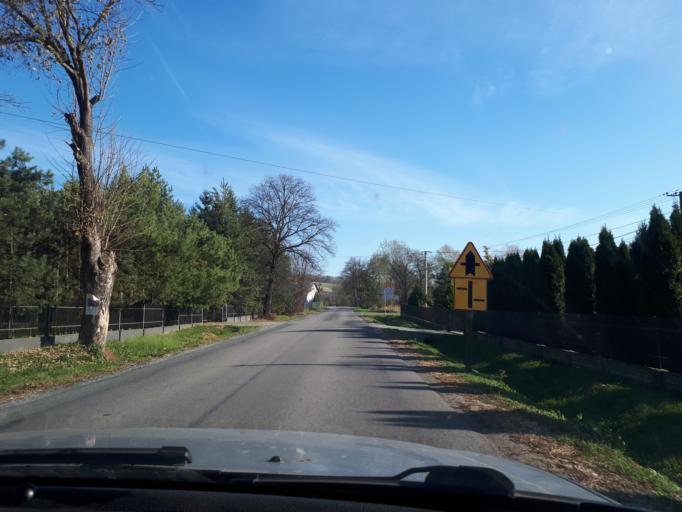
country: PL
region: Subcarpathian Voivodeship
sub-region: Powiat debicki
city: Debica
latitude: 50.0046
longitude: 21.4003
